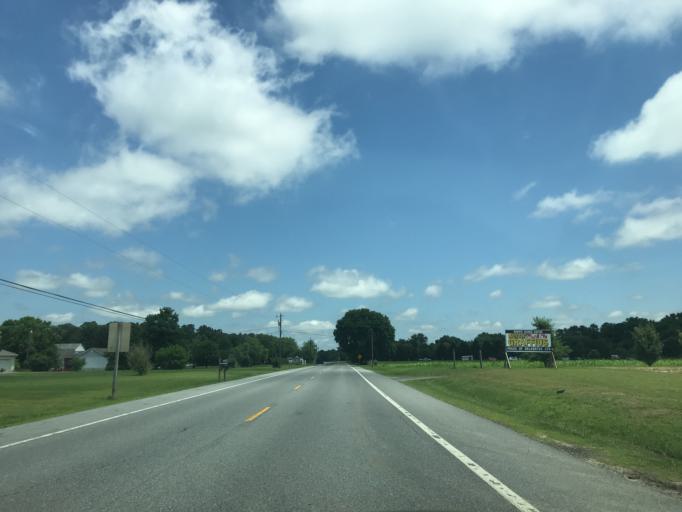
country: US
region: Maryland
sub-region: Caroline County
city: Federalsburg
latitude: 38.7048
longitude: -75.7526
